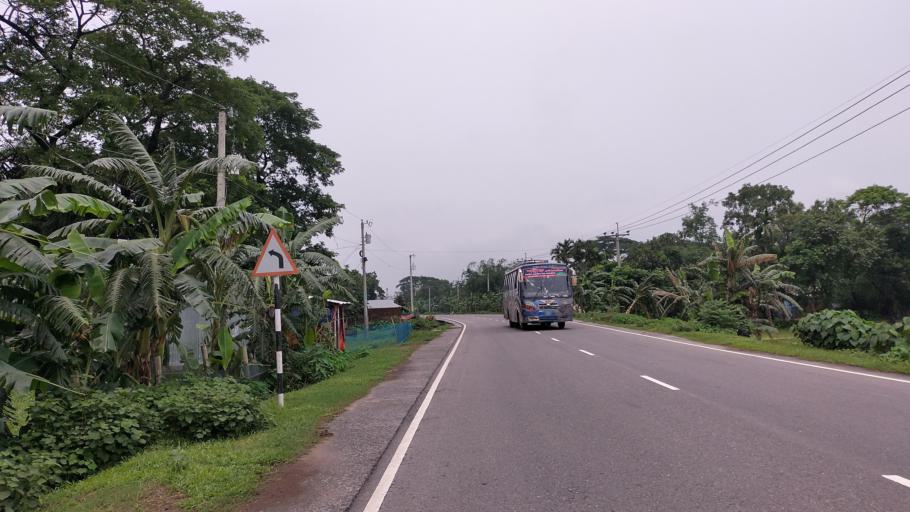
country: BD
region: Dhaka
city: Netrakona
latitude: 24.8516
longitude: 90.6220
